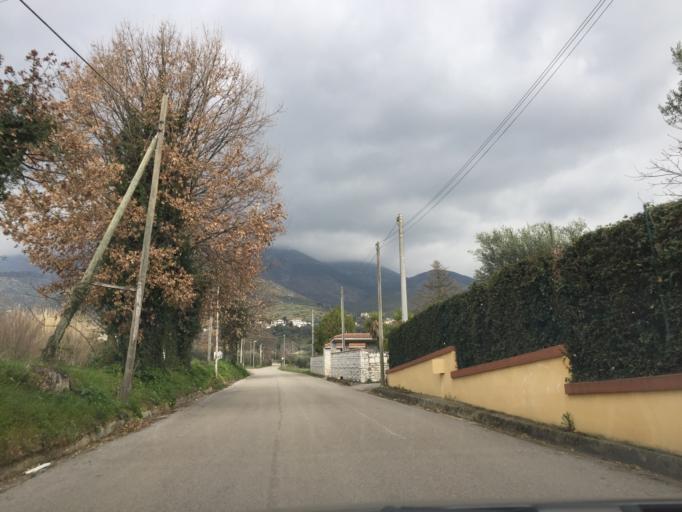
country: IT
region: Latium
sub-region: Provincia di Frosinone
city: Piedimonte San Germano Alta
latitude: 41.5004
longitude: 13.7439
